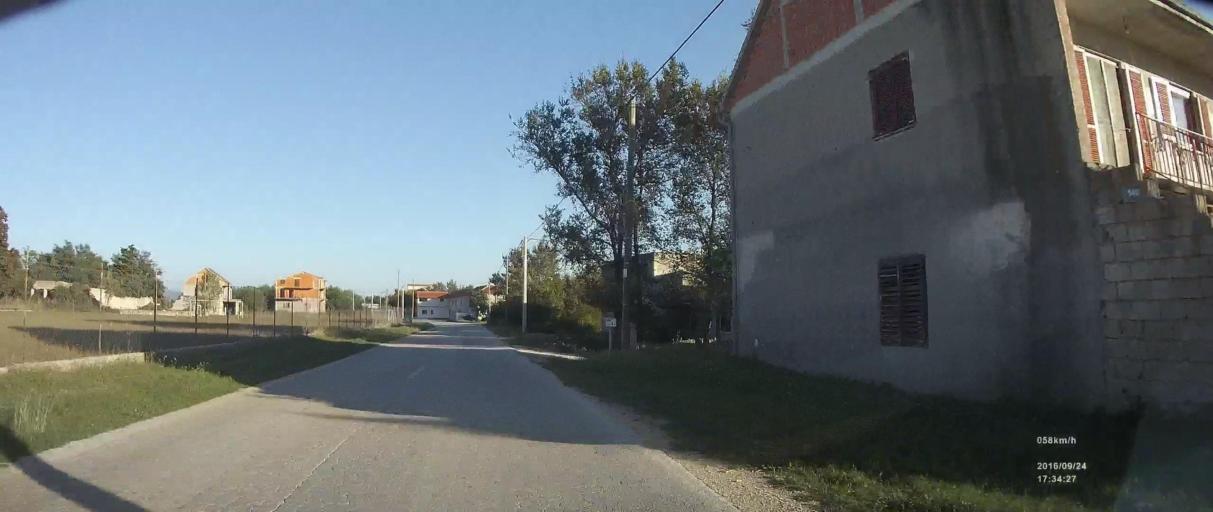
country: HR
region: Zadarska
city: Posedarje
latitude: 44.1670
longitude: 15.4598
